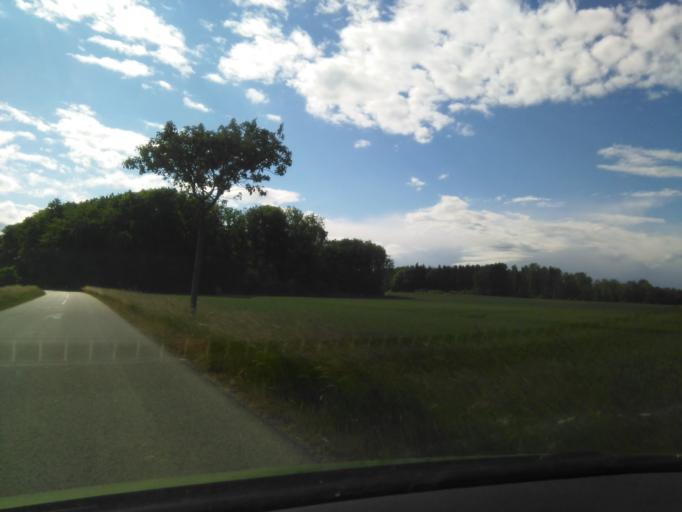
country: DK
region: Capital Region
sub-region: Bornholm Kommune
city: Nexo
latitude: 55.1244
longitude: 15.0727
